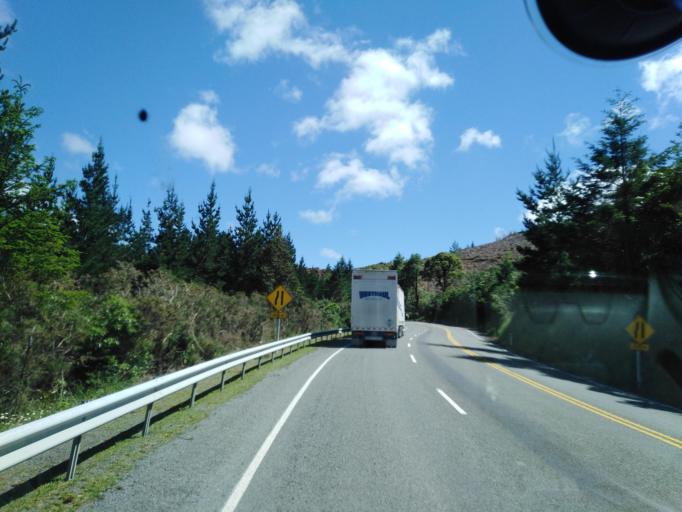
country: NZ
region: Nelson
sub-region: Nelson City
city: Nelson
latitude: -41.1935
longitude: 173.5575
